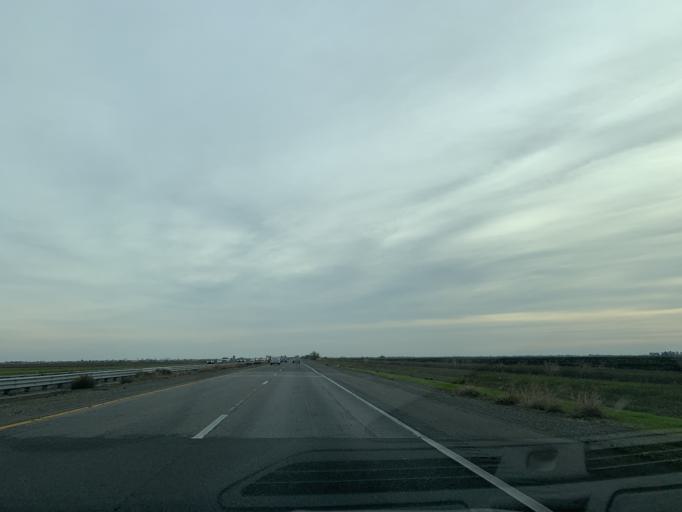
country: US
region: California
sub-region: Sacramento County
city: Elverta
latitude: 38.7025
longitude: -121.5404
